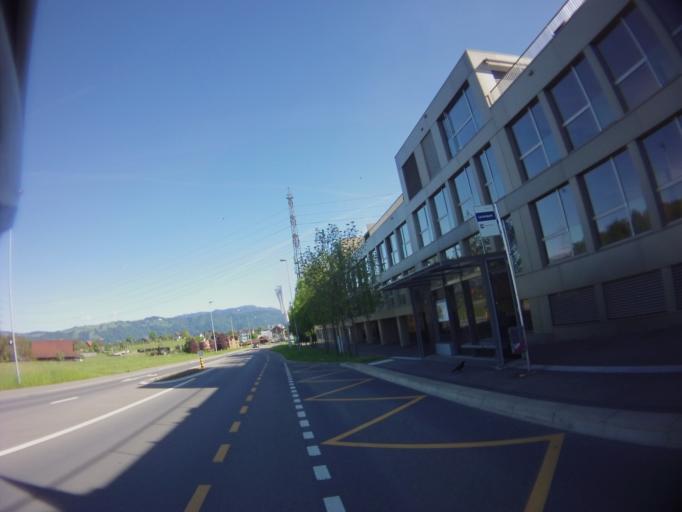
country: CH
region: Zug
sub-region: Zug
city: Cham
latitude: 47.1920
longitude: 8.4563
